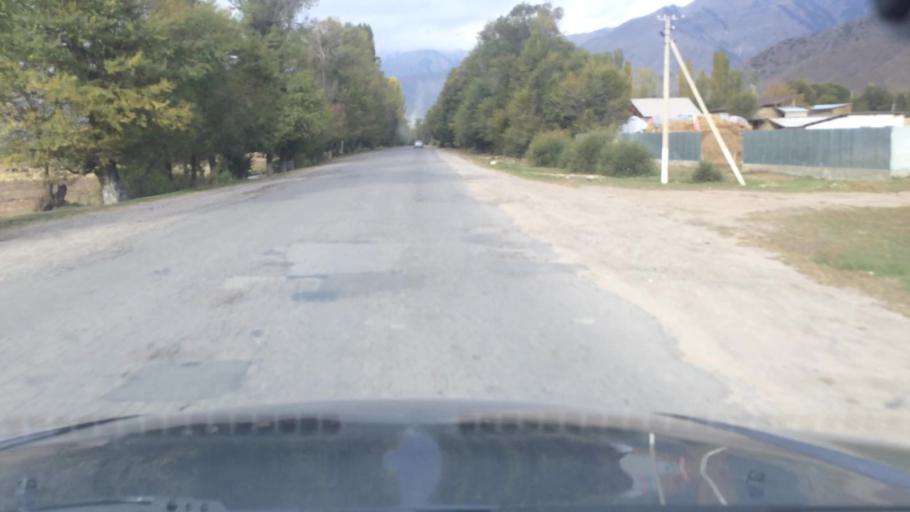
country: KG
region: Ysyk-Koel
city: Tyup
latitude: 42.7826
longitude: 78.2817
